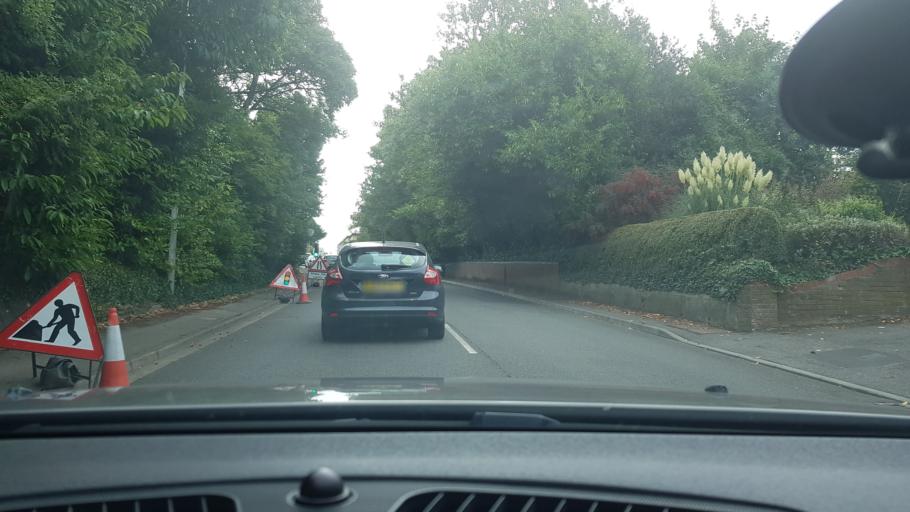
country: GB
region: England
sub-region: West Berkshire
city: Greenham
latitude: 51.3905
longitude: -1.3140
